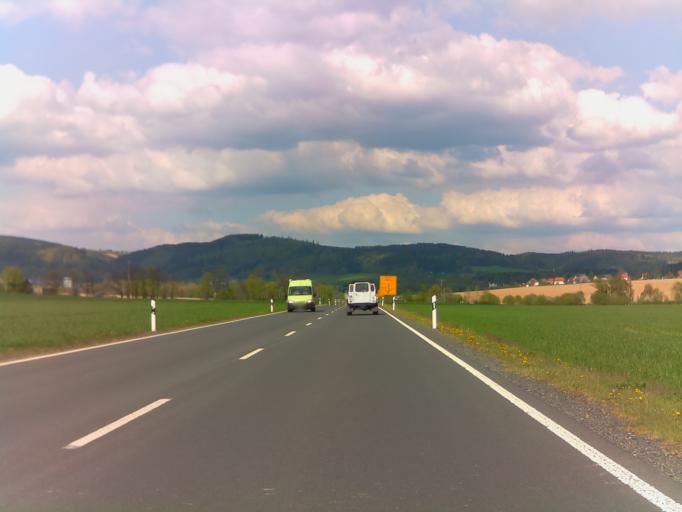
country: DE
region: Thuringia
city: Sonneberg
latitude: 50.3308
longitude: 11.1909
